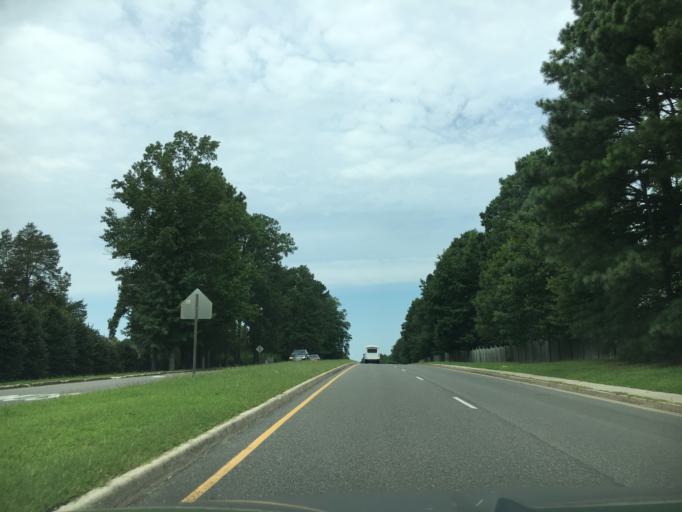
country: US
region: Virginia
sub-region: Henrico County
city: Short Pump
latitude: 37.6083
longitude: -77.6316
